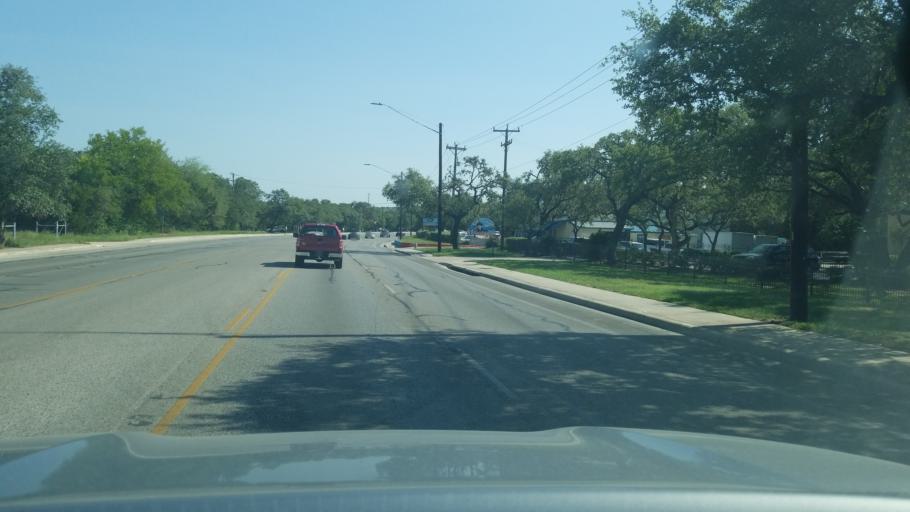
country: US
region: Texas
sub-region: Bexar County
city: Hollywood Park
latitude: 29.5926
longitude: -98.5117
